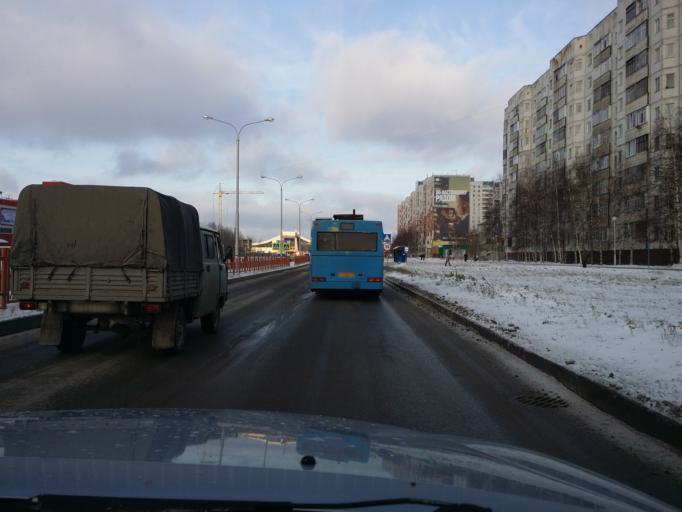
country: RU
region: Khanty-Mansiyskiy Avtonomnyy Okrug
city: Nizhnevartovsk
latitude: 60.9472
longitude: 76.6041
